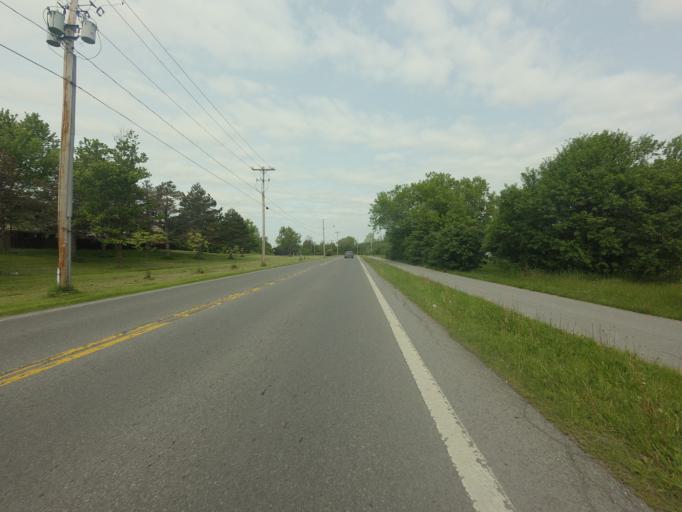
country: US
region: New York
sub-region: Jefferson County
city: Watertown
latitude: 43.9777
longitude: -75.8814
